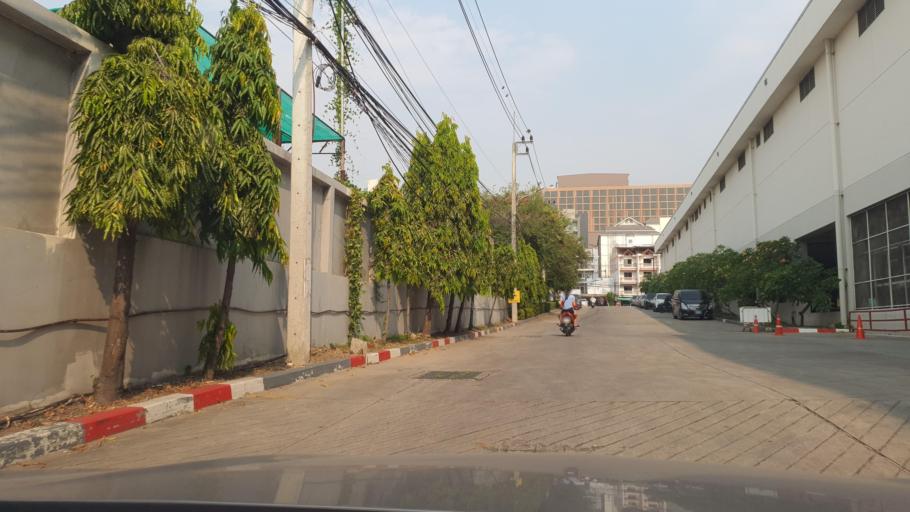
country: TH
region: Chon Buri
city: Phatthaya
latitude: 12.9358
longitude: 100.8946
